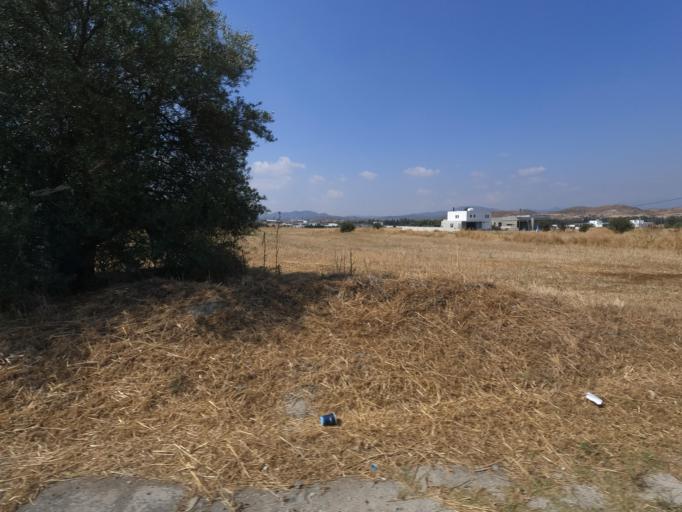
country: CY
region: Lefkosia
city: Lympia
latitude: 35.0009
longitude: 33.4492
